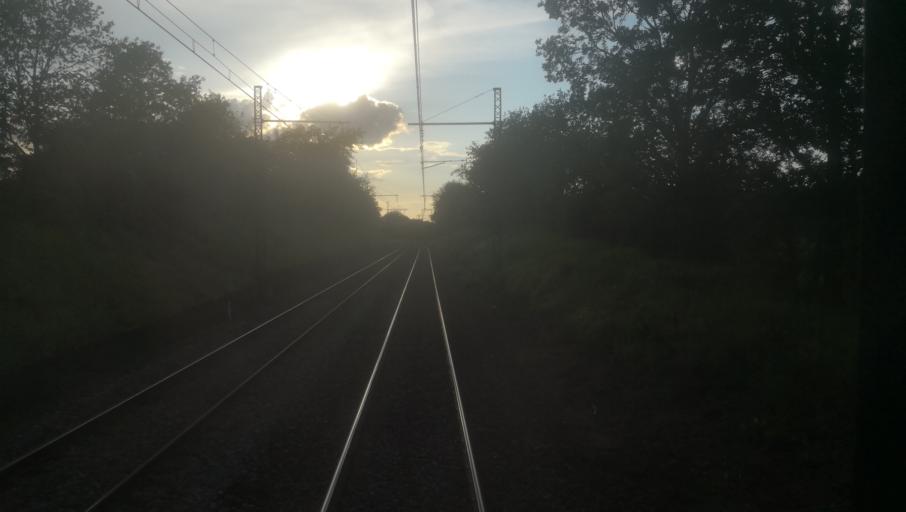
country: FR
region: Centre
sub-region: Departement de l'Indre
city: Le Pechereau
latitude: 46.4991
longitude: 1.5175
